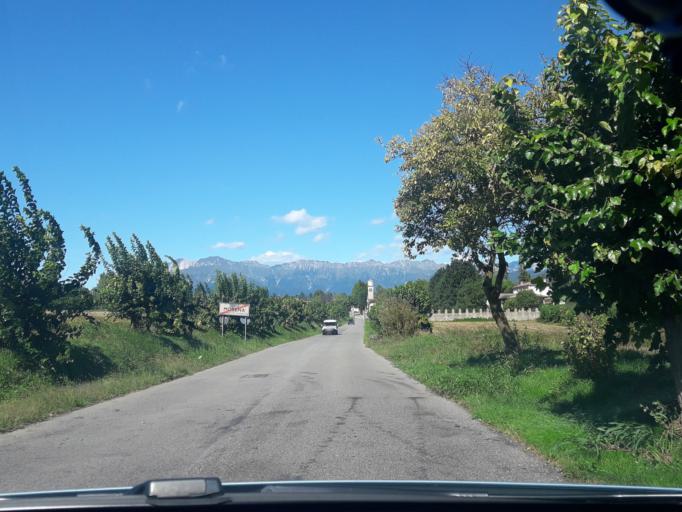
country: IT
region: Friuli Venezia Giulia
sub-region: Provincia di Udine
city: Reana del Roiale
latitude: 46.1459
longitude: 13.2153
